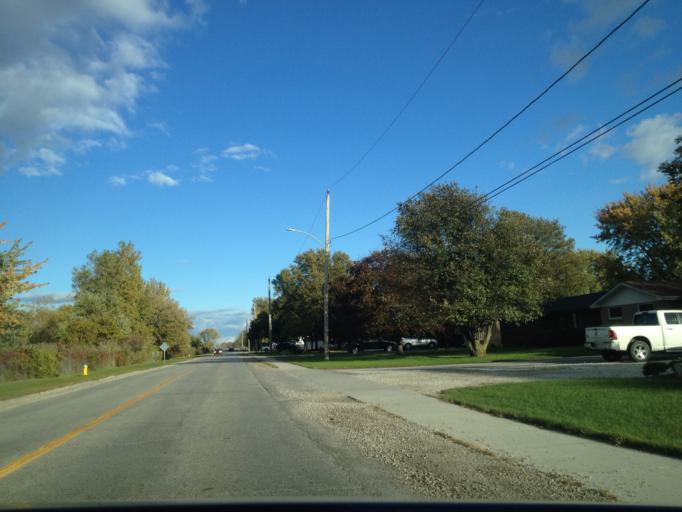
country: US
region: Michigan
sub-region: Wayne County
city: Grosse Pointe Farms
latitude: 42.2964
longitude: -82.6930
